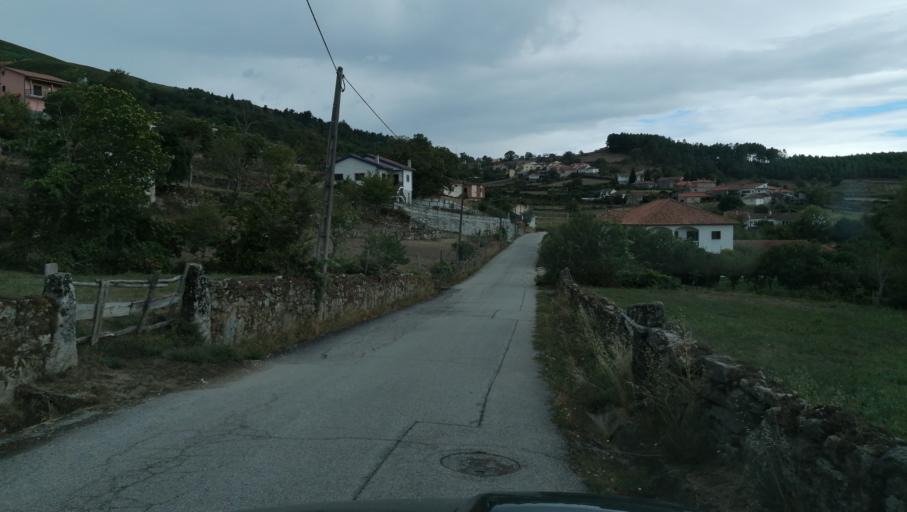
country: PT
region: Vila Real
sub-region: Vila Pouca de Aguiar
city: Vila Pouca de Aguiar
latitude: 41.5597
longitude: -7.6490
